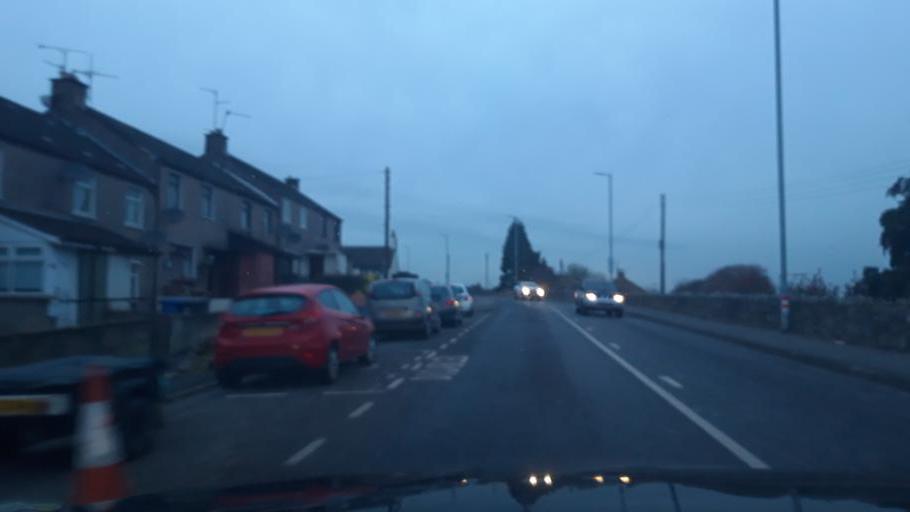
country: GB
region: Northern Ireland
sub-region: Newry and Mourne District
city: Newry
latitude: 54.1790
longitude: -6.3479
